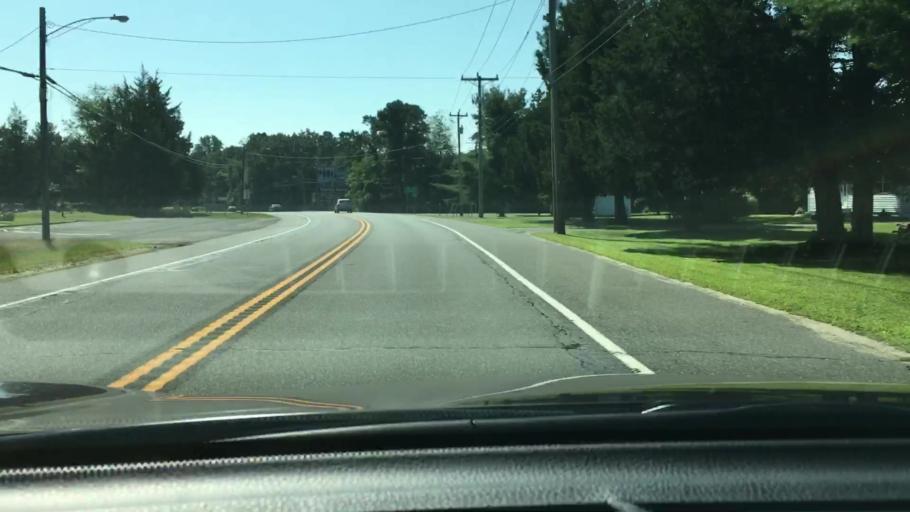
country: US
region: New Jersey
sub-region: Cumberland County
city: Laurel Lake
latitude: 39.3709
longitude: -74.9425
